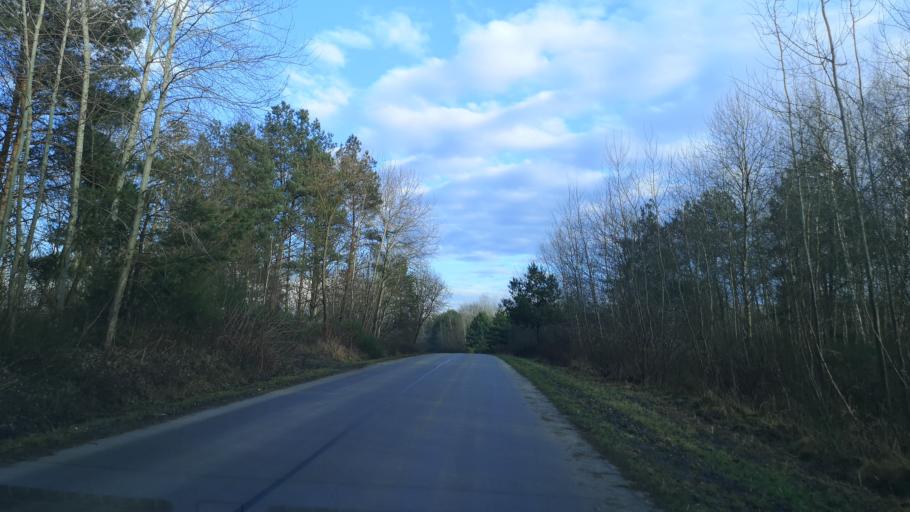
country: PL
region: Subcarpathian Voivodeship
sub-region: Powiat lezajski
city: Piskorowice
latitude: 50.2430
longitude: 22.5400
